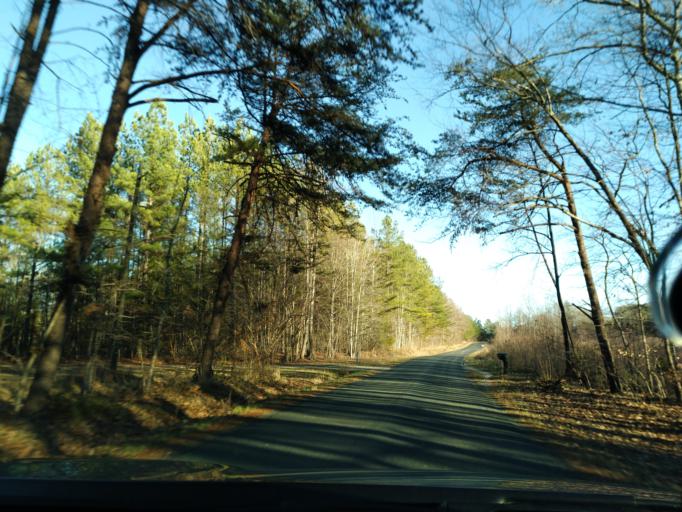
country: US
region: Virginia
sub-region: Buckingham County
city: Buckingham
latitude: 37.3706
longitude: -78.6210
